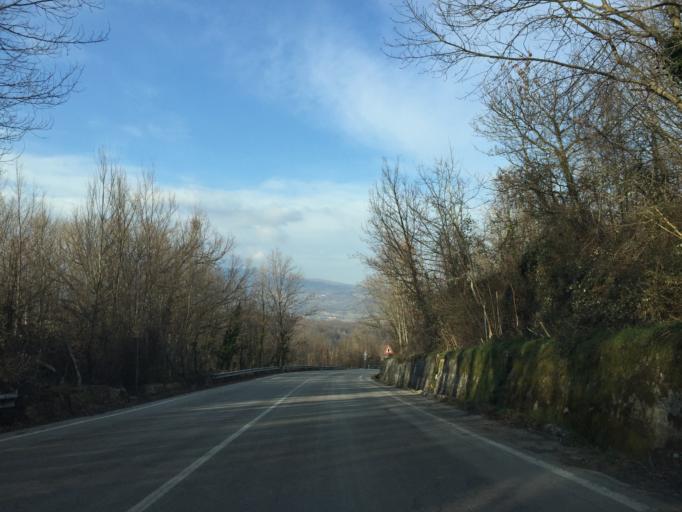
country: IT
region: Molise
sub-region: Provincia di Campobasso
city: San Massimo
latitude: 41.4886
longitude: 14.4063
